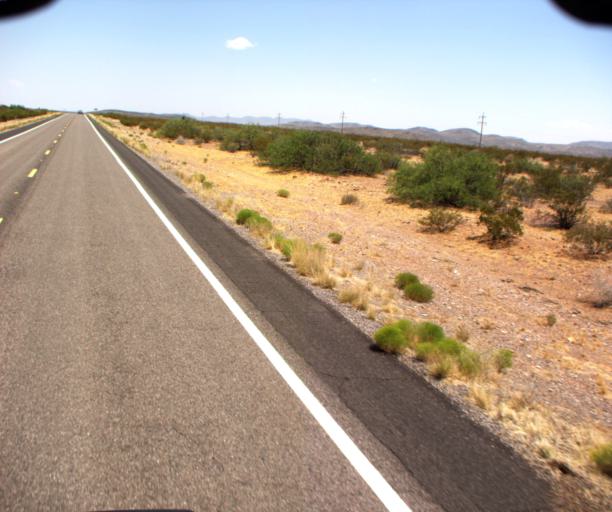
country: US
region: Arizona
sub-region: Graham County
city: Swift Trail Junction
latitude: 32.7616
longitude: -109.4432
